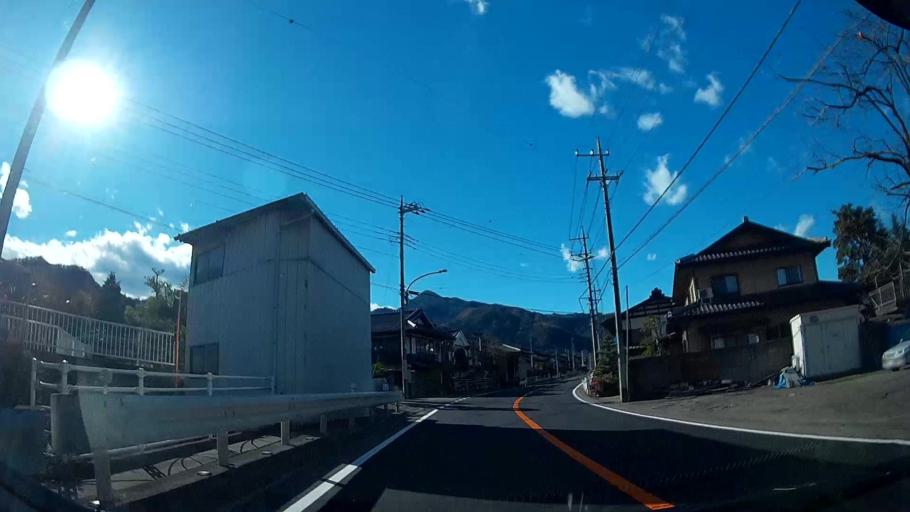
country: JP
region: Yamanashi
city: Otsuki
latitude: 35.5964
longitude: 138.8875
